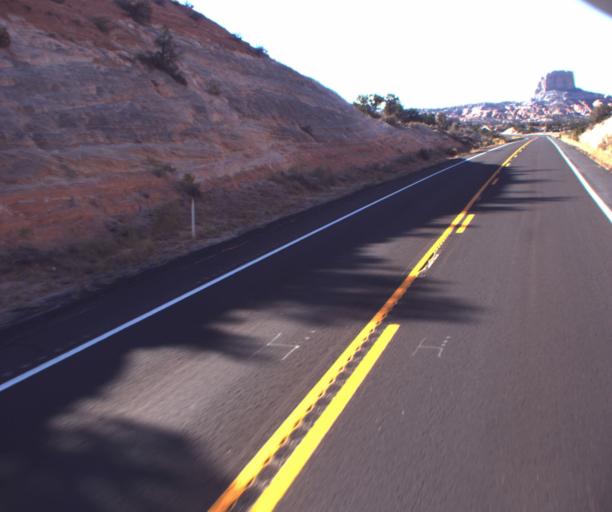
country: US
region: Arizona
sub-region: Coconino County
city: Kaibito
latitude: 36.5915
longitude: -110.8955
